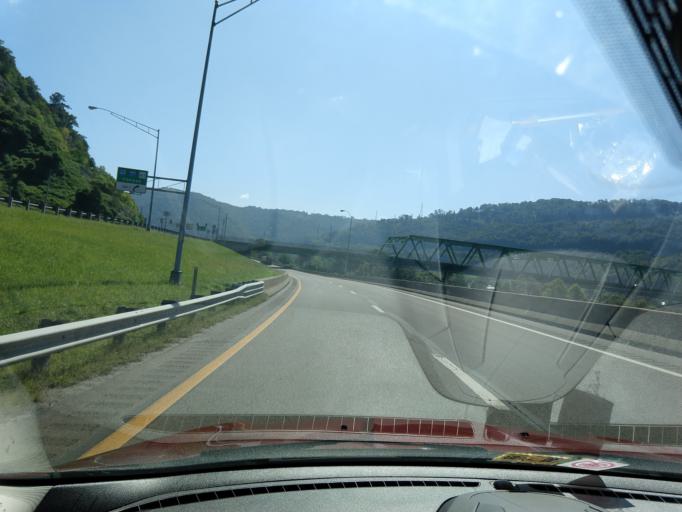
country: US
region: West Virginia
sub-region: Kanawha County
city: Chesapeake
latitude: 38.1993
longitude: -81.4941
